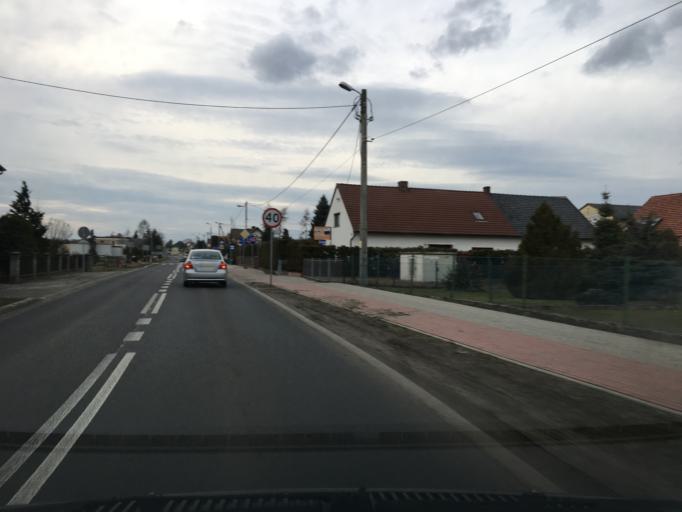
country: PL
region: Opole Voivodeship
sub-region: Powiat krapkowicki
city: Januszkowice
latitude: 50.3917
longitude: 18.1373
